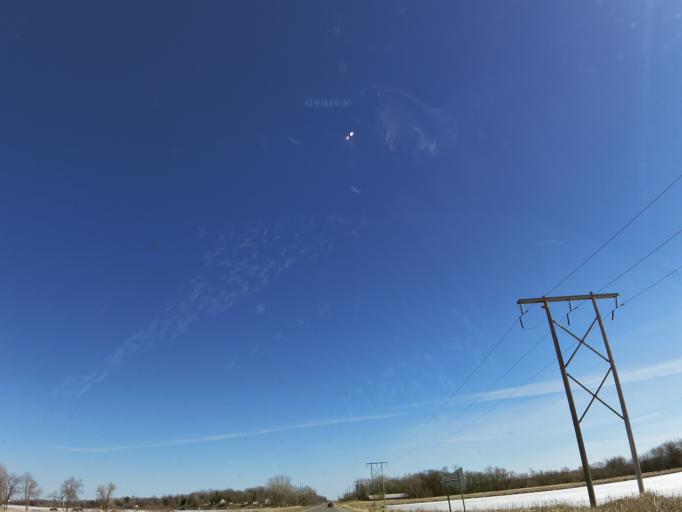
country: US
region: Minnesota
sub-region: Wright County
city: Maple Lake
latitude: 45.2267
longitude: -93.9820
